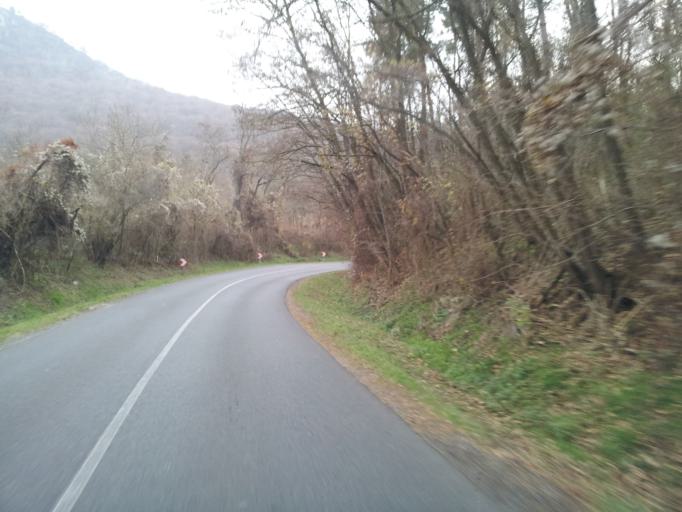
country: HU
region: Zala
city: Cserszegtomaj
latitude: 46.8730
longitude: 17.2202
